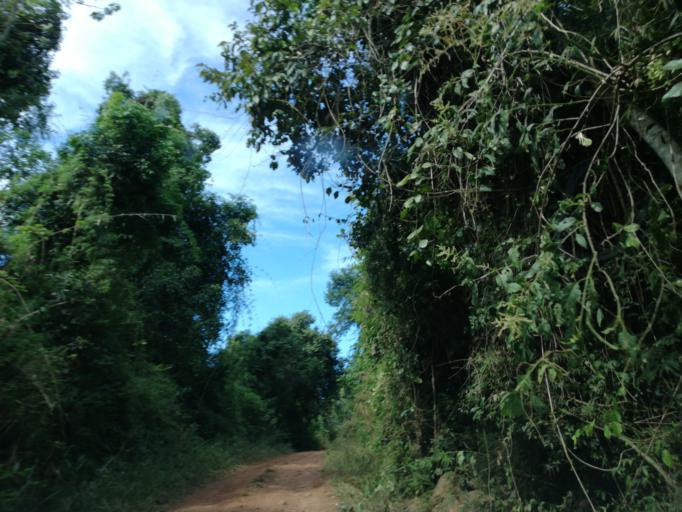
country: AR
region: Misiones
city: Dos de Mayo
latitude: -27.0141
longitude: -54.4331
